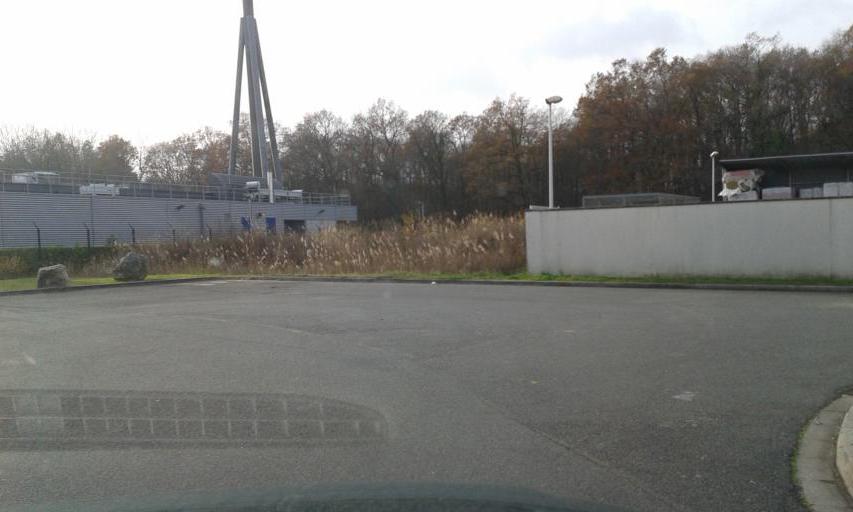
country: FR
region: Centre
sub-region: Departement du Loiret
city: Saran
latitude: 47.9481
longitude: 1.8587
